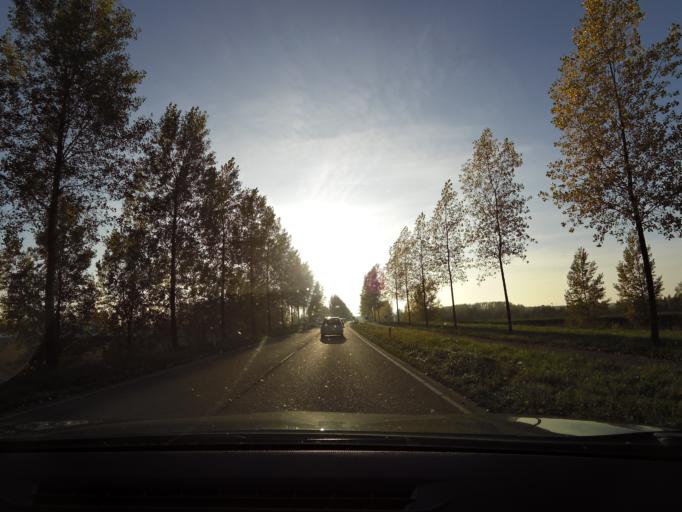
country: NL
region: South Holland
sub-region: Gemeente Strijen
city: Strijen
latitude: 51.6960
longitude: 4.6542
